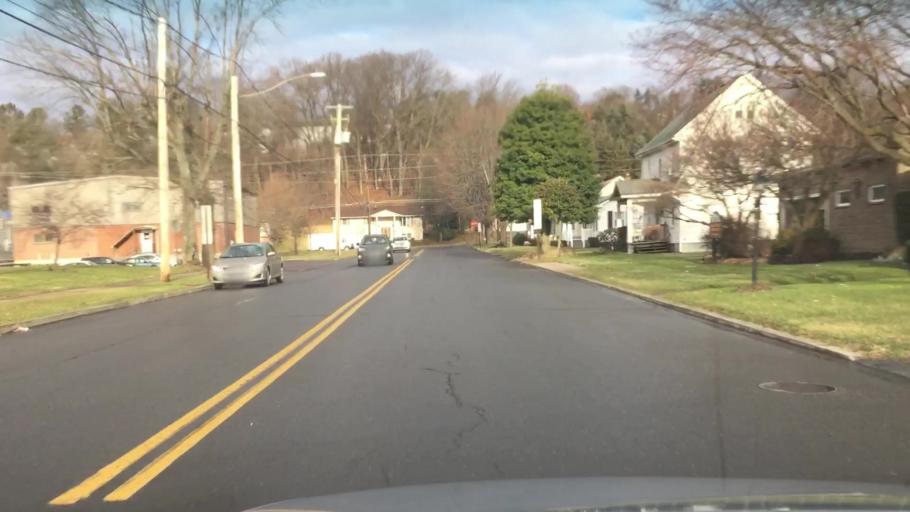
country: US
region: Pennsylvania
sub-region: Columbia County
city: Bloomsburg
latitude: 41.0039
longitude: -76.4422
